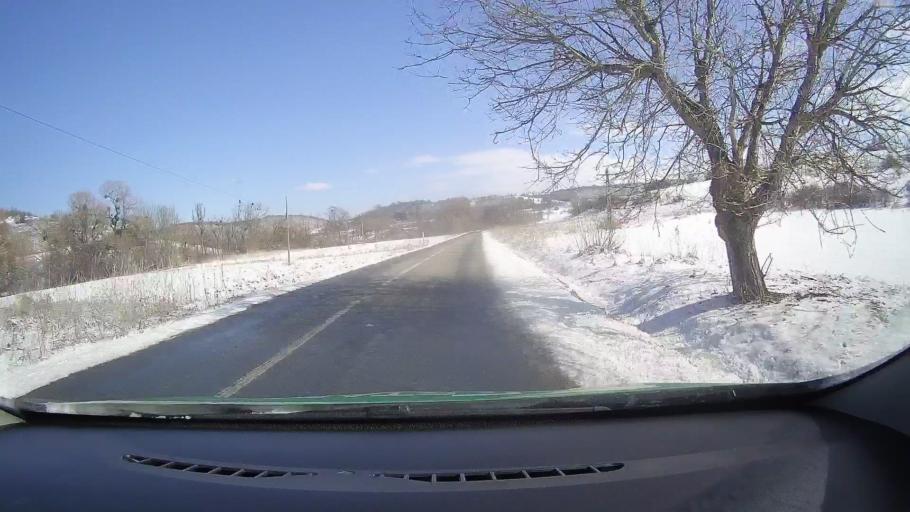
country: RO
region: Sibiu
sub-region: Comuna Mihaileni
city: Mihaileni
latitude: 46.0157
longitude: 24.3793
